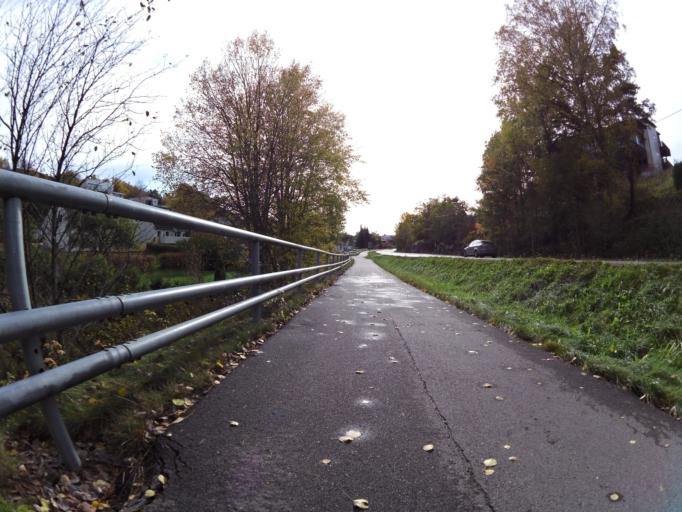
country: NO
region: Ostfold
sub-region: Fredrikstad
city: Fredrikstad
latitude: 59.2233
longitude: 10.9102
